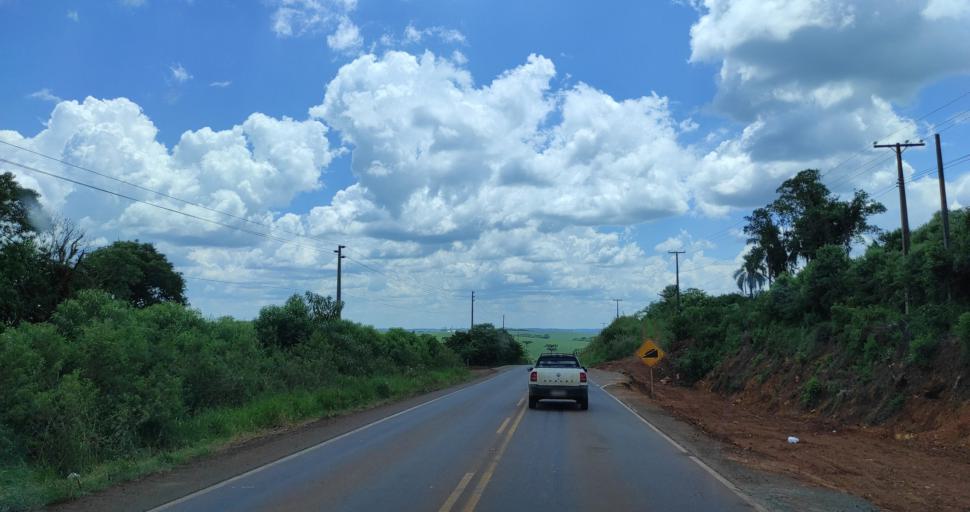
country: BR
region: Santa Catarina
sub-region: Xanxere
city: Xanxere
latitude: -26.8314
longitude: -52.4149
